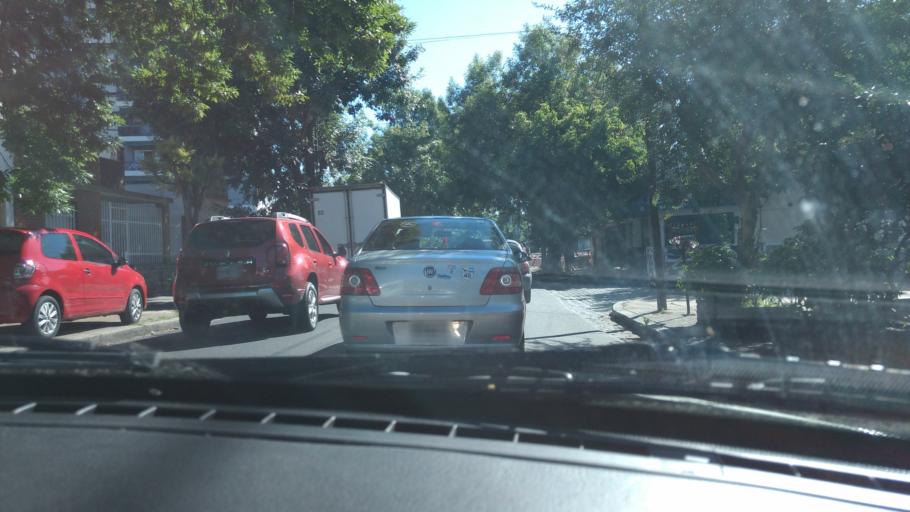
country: AR
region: Buenos Aires F.D.
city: Villa Santa Rita
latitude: -34.6240
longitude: -58.5238
